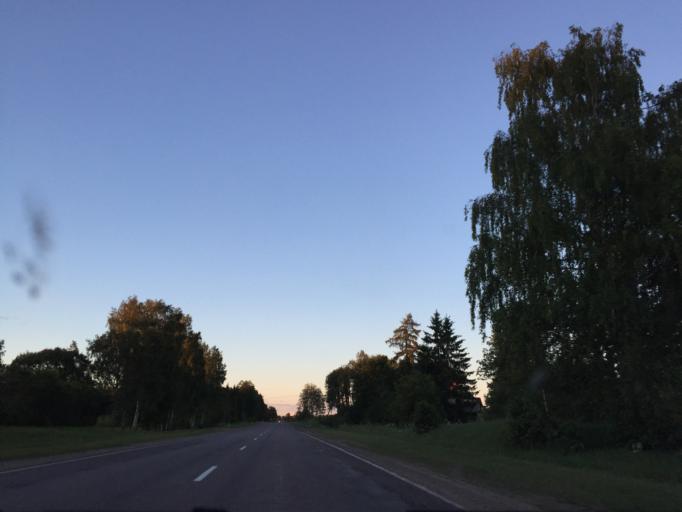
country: LV
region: Jaunpiebalga
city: Jaunpiebalga
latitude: 57.4459
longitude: 26.2118
